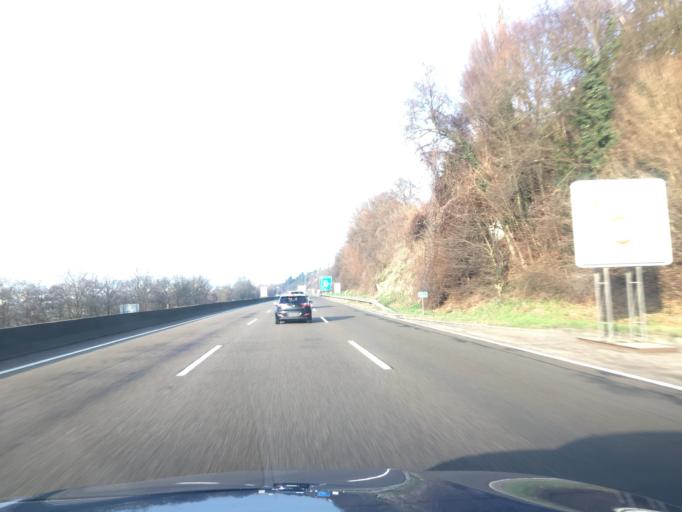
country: DE
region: Rheinland-Pfalz
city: Weitersburg
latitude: 50.4095
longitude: 7.5937
